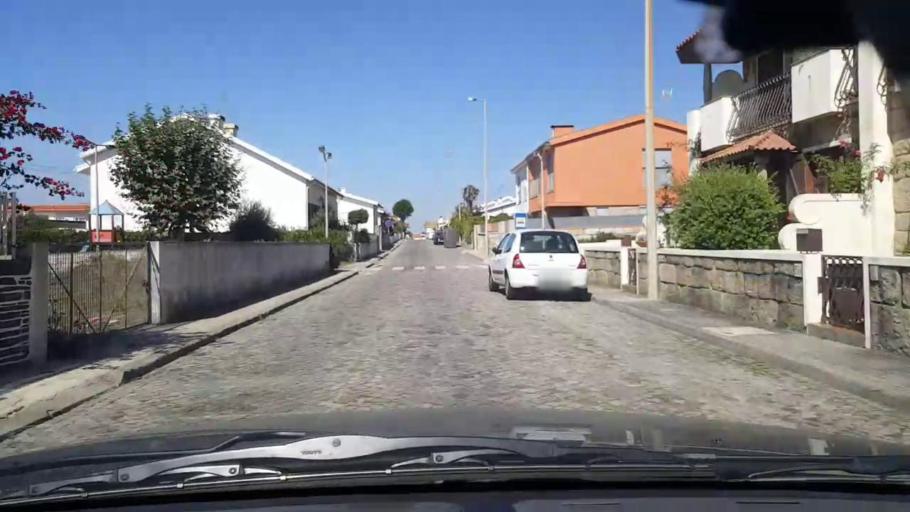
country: PT
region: Porto
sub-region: Vila do Conde
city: Arvore
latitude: 41.3070
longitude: -8.7355
